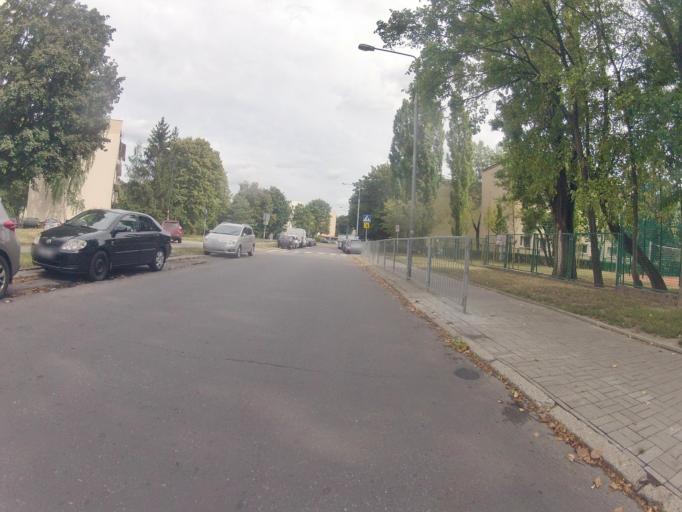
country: PL
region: Masovian Voivodeship
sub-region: Warszawa
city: Mokotow
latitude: 52.1906
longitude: 21.0065
